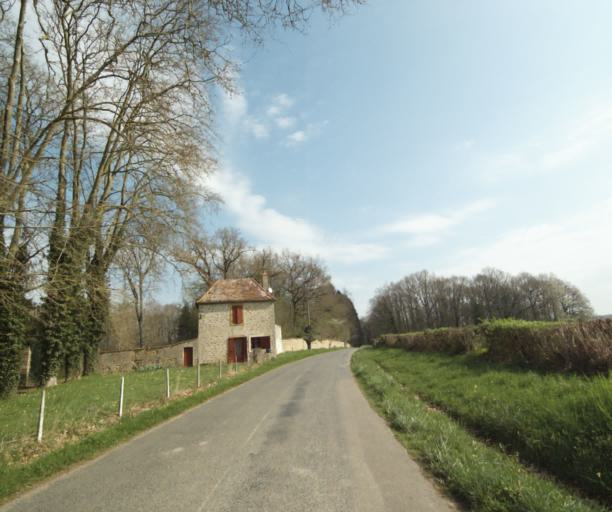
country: FR
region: Bourgogne
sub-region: Departement de Saone-et-Loire
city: Palinges
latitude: 46.5175
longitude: 4.2086
